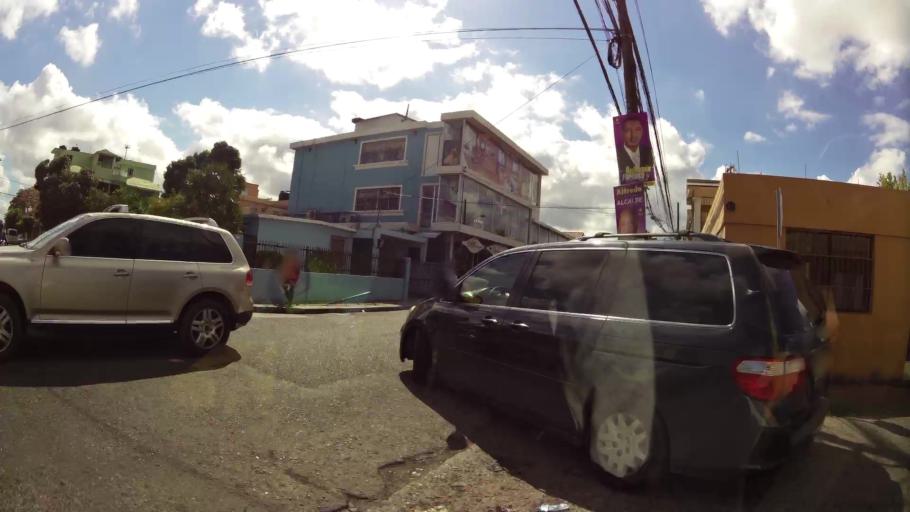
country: DO
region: Santo Domingo
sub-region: Santo Domingo
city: Santo Domingo Este
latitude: 18.5082
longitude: -69.8489
